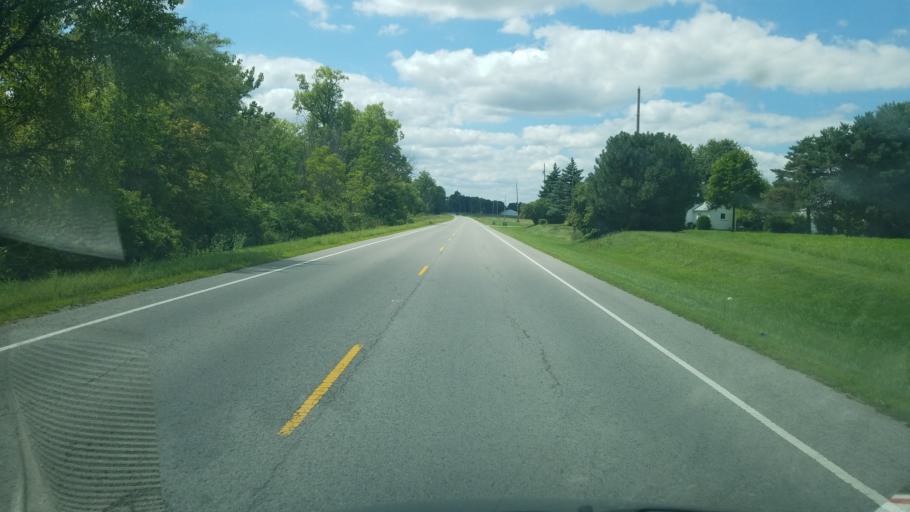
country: US
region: Ohio
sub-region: Henry County
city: Napoleon
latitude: 41.4112
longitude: -84.0664
